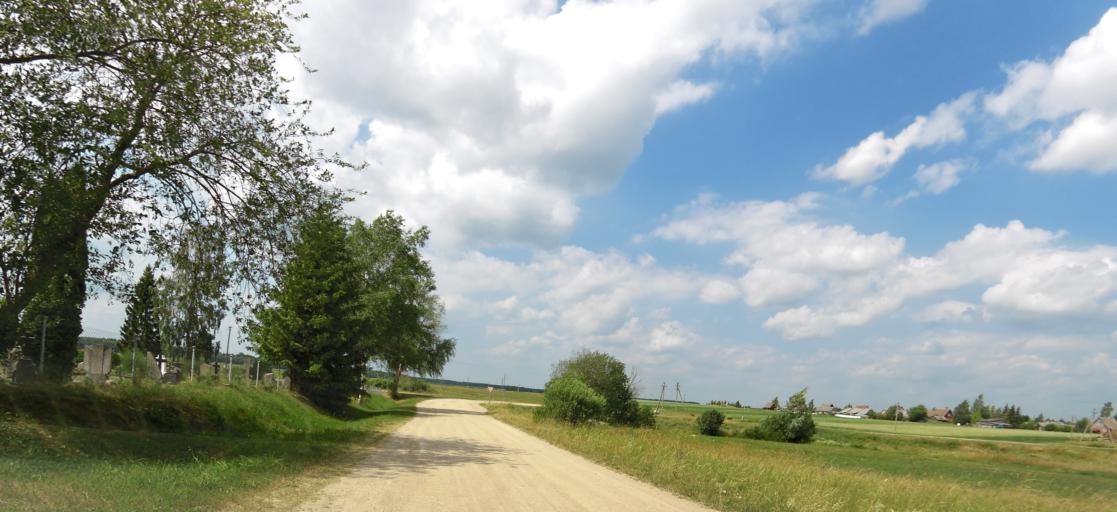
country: LT
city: Obeliai
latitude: 56.1425
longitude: 25.0461
